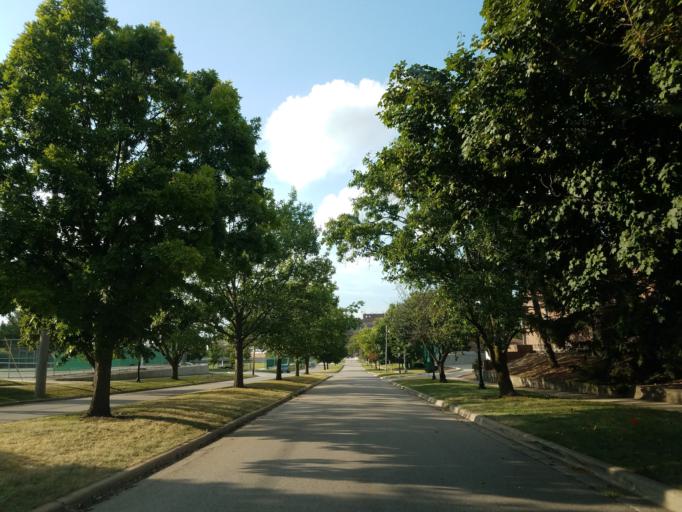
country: US
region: Illinois
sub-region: McLean County
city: Bloomington
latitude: 40.4940
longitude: -88.9908
